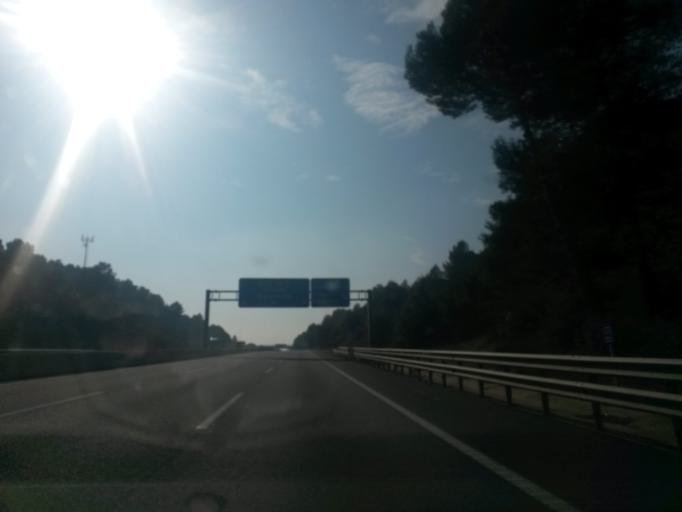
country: ES
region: Catalonia
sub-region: Provincia de Girona
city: Bascara
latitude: 42.1359
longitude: 2.9161
